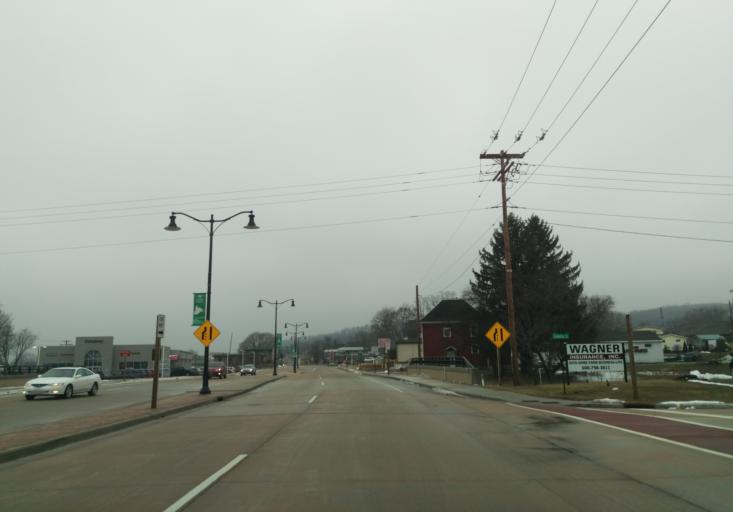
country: US
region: Wisconsin
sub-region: Dane County
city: Cross Plains
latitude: 43.1117
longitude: -89.6456
